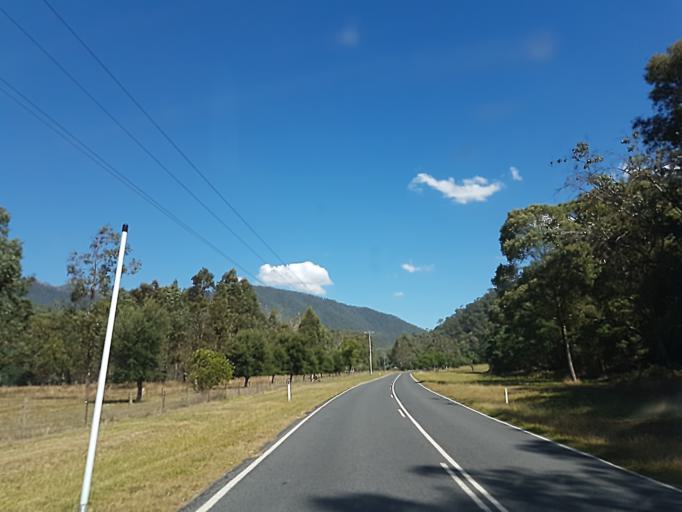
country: AU
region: Victoria
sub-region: Alpine
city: Mount Beauty
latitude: -36.8403
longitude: 147.0784
